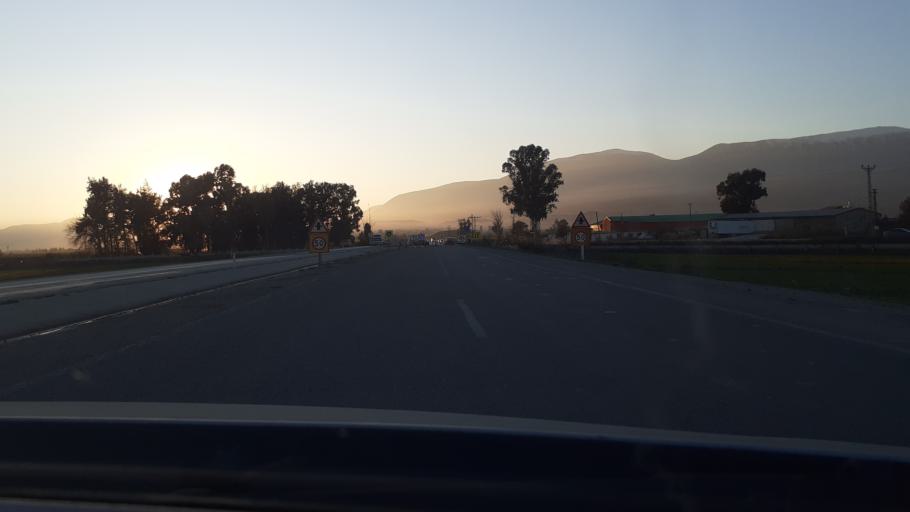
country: TR
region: Hatay
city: Kirikhan
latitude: 36.5054
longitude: 36.4163
